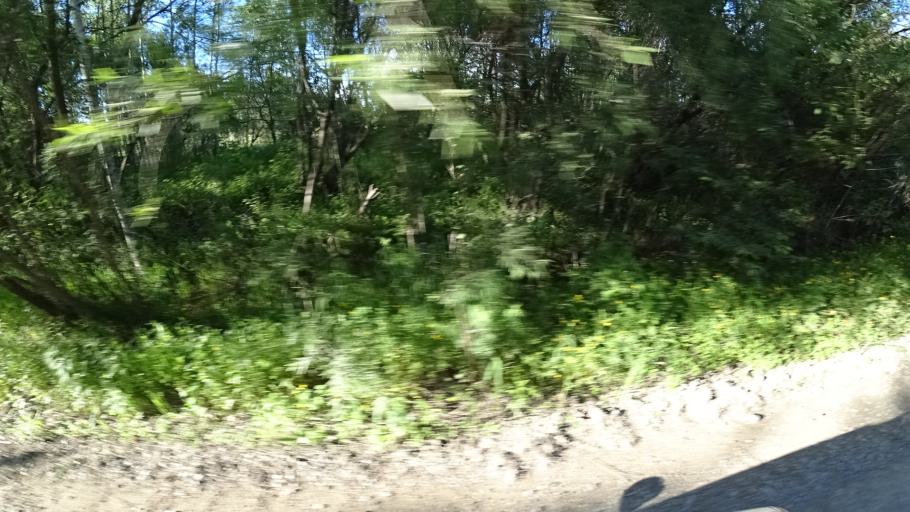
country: RU
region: Khabarovsk Krai
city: Khor
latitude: 47.8440
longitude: 134.9502
